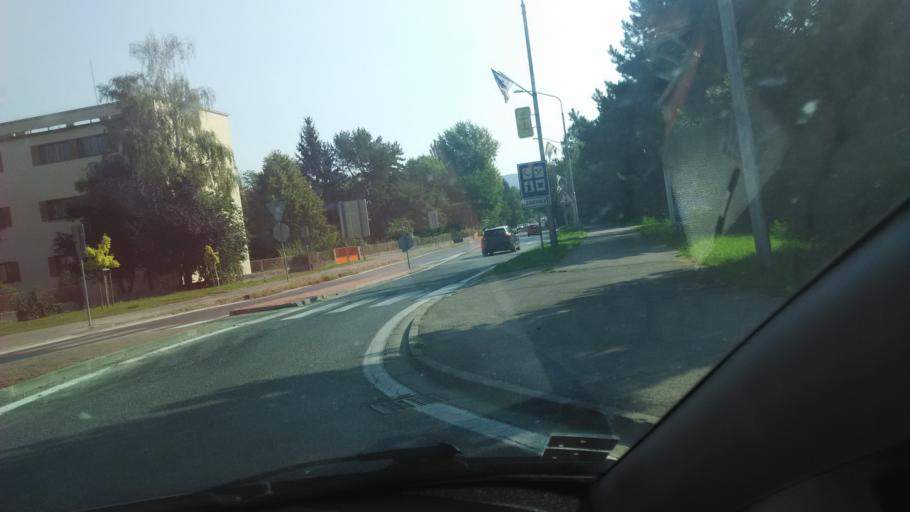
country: SK
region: Trnavsky
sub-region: Okres Trnava
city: Piestany
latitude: 48.5861
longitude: 17.8251
